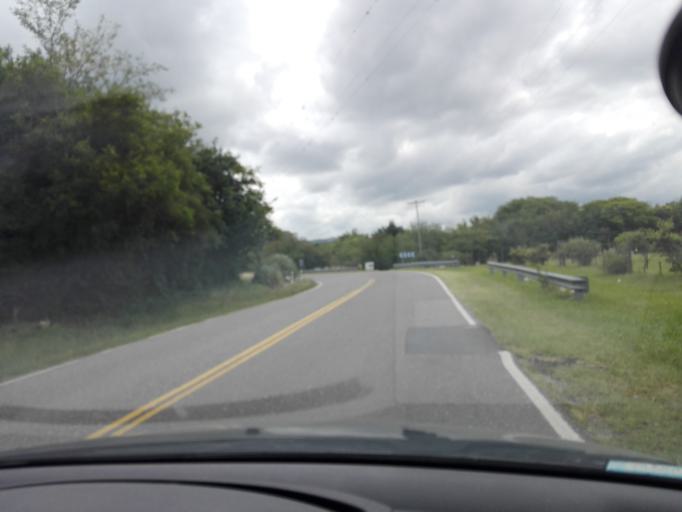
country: AR
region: Cordoba
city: Alta Gracia
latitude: -31.5855
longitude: -64.4779
